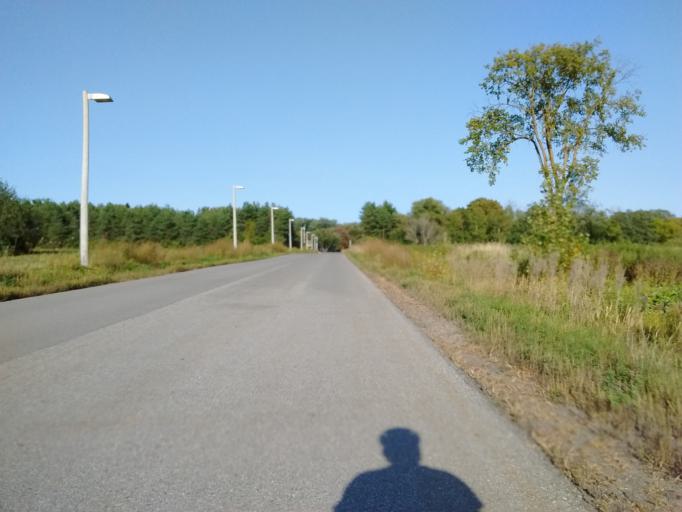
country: CA
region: Ontario
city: Ottawa
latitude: 45.4400
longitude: -75.6150
